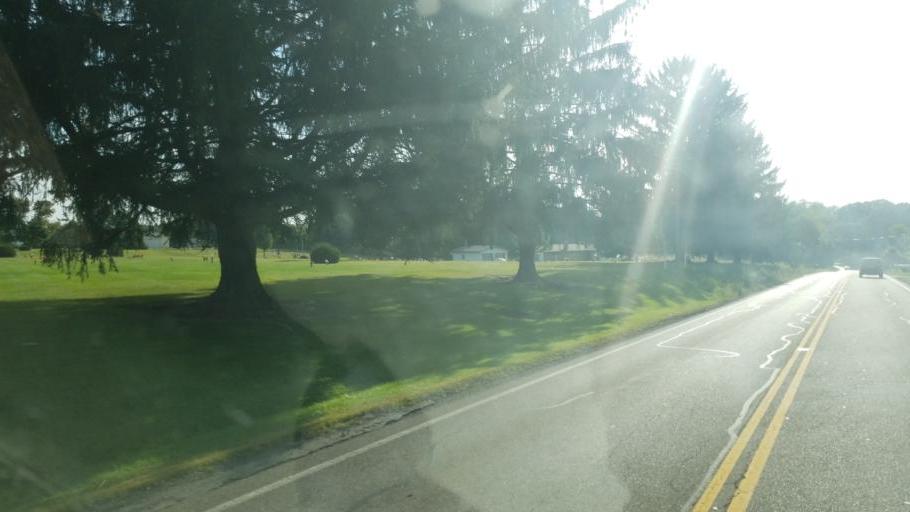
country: US
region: Ohio
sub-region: Knox County
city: Gambier
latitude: 40.4120
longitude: -82.4206
